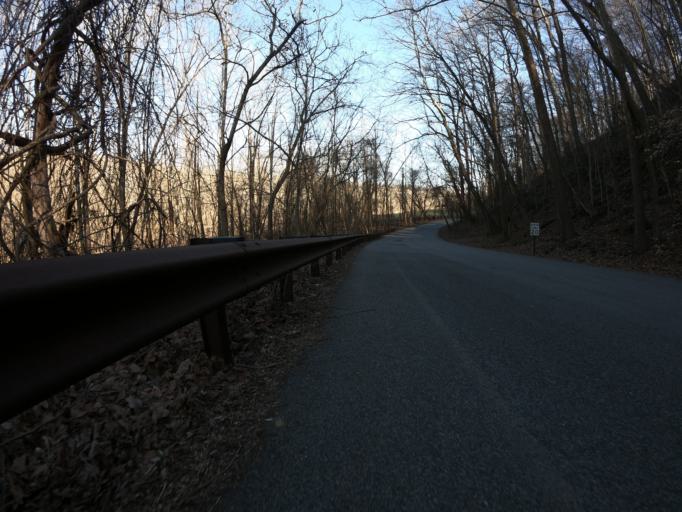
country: US
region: Maryland
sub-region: Howard County
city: West Elkridge
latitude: 39.2284
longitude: -76.7282
